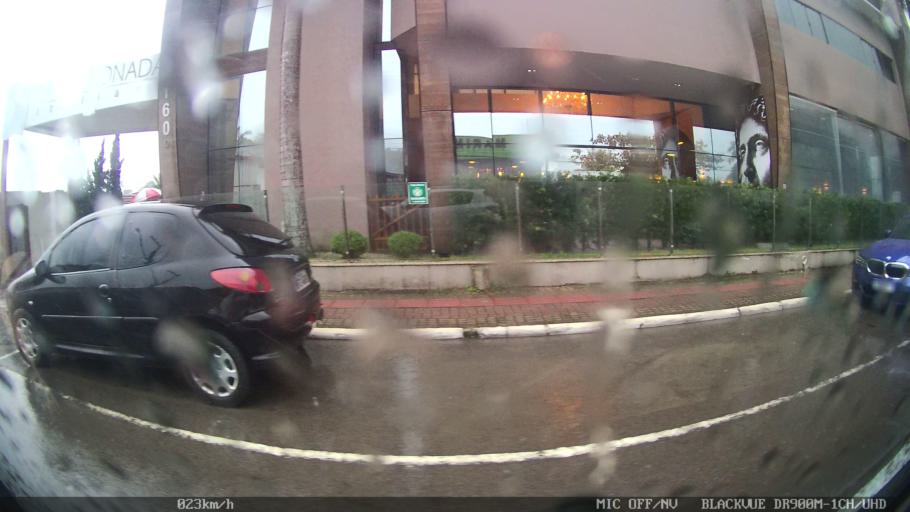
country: BR
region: Santa Catarina
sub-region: Balneario Camboriu
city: Balneario Camboriu
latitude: -27.0078
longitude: -48.6240
